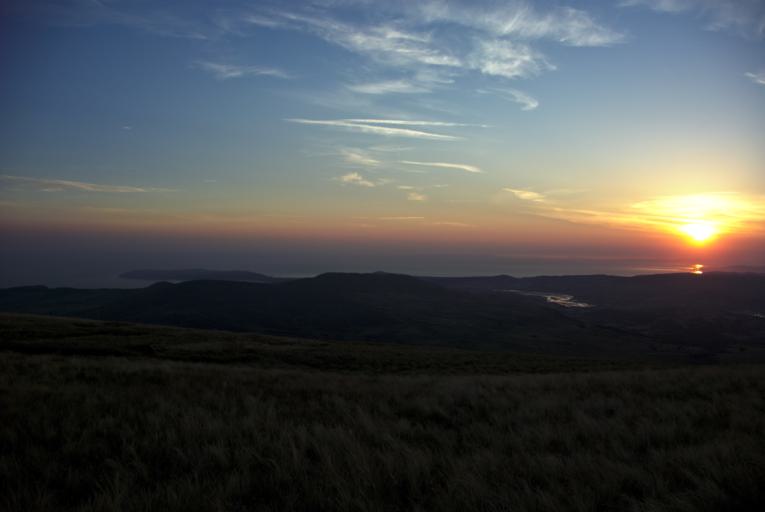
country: GB
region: Wales
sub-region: Conwy
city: Llanfairfechan
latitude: 53.2082
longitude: -3.9352
